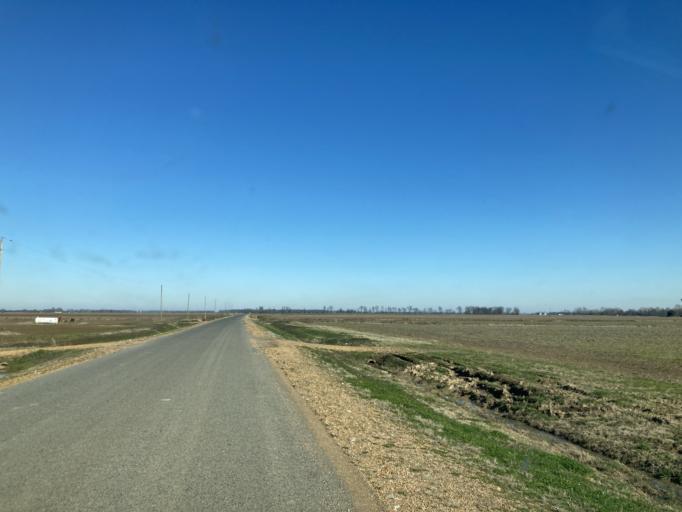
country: US
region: Mississippi
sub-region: Yazoo County
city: Yazoo City
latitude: 32.9715
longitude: -90.6053
